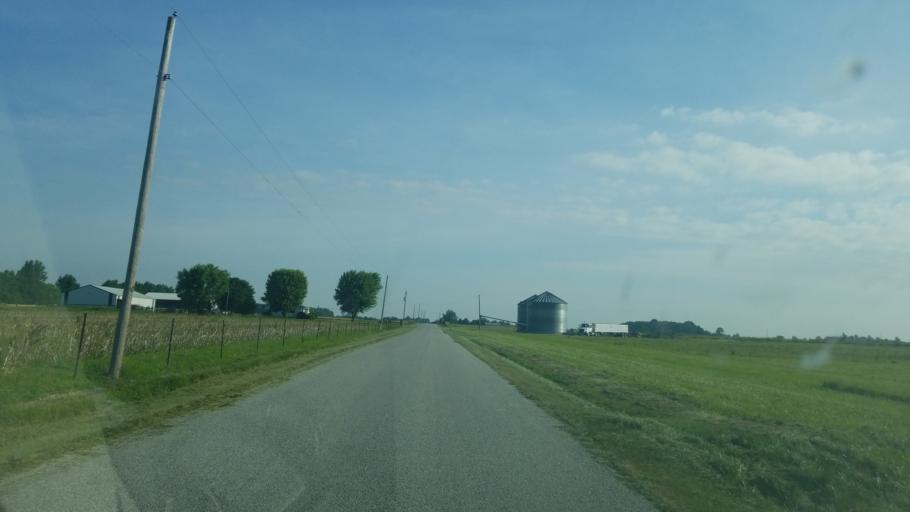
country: US
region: Ohio
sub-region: Hancock County
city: Arlington
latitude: 40.8071
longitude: -83.6706
